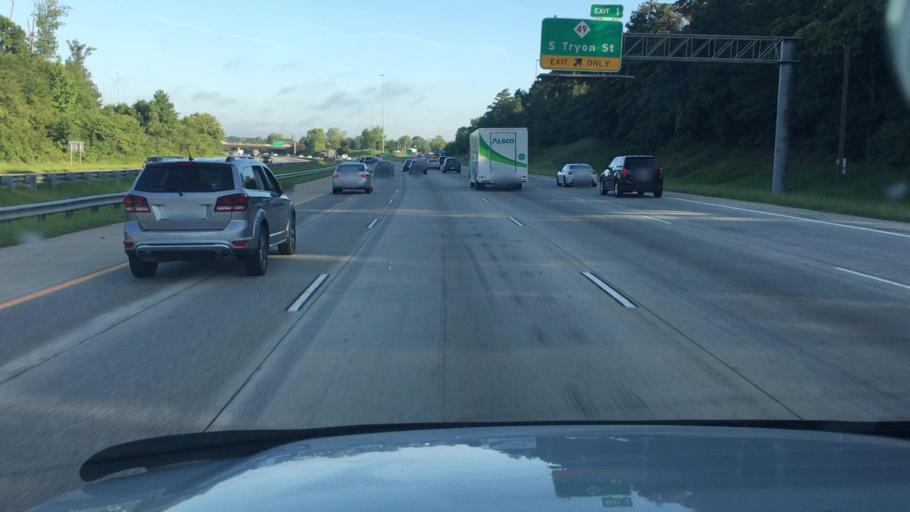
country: US
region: North Carolina
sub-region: Mecklenburg County
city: Pineville
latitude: 35.1371
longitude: -80.9264
